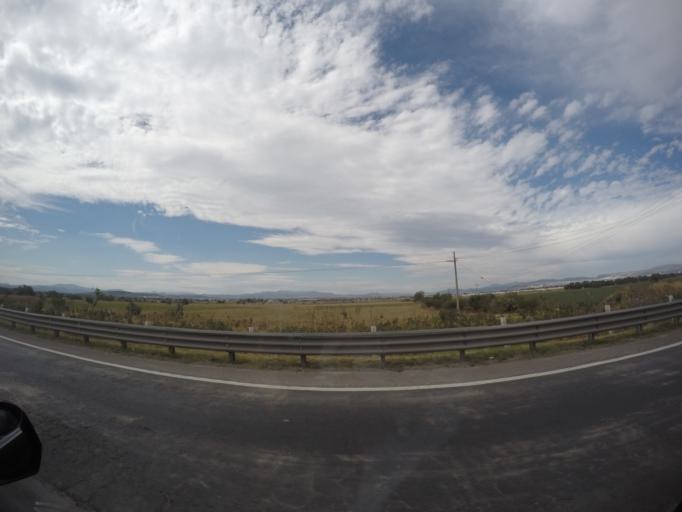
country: MX
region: Queretaro
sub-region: Queretaro
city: Rancho Bellavista [Fraccionamiento]
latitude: 20.5758
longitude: -100.4434
